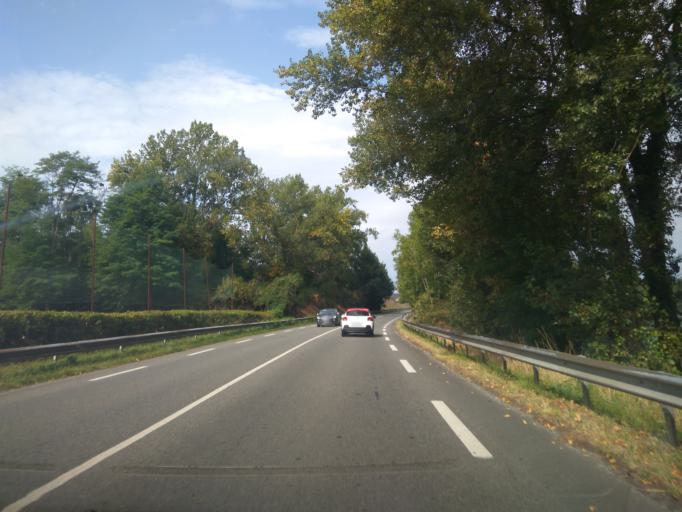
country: FR
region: Aquitaine
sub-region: Departement des Pyrenees-Atlantiques
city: Artiguelouve
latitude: 43.3074
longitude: -0.4446
